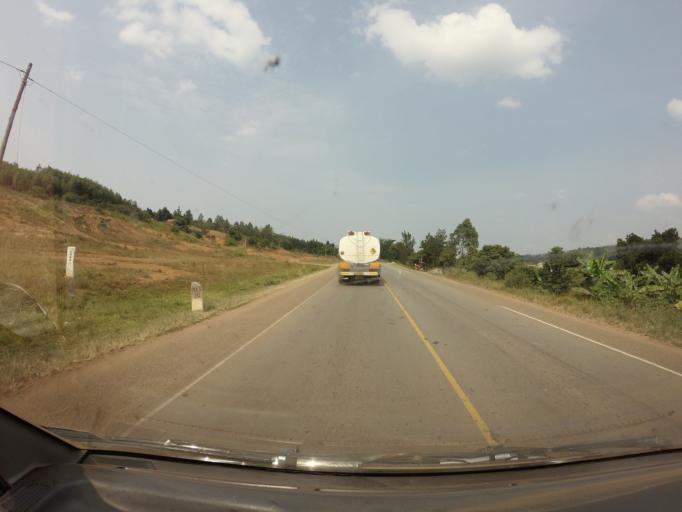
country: UG
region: Central Region
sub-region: Lwengo District
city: Lwengo
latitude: -0.3930
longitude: 31.3325
